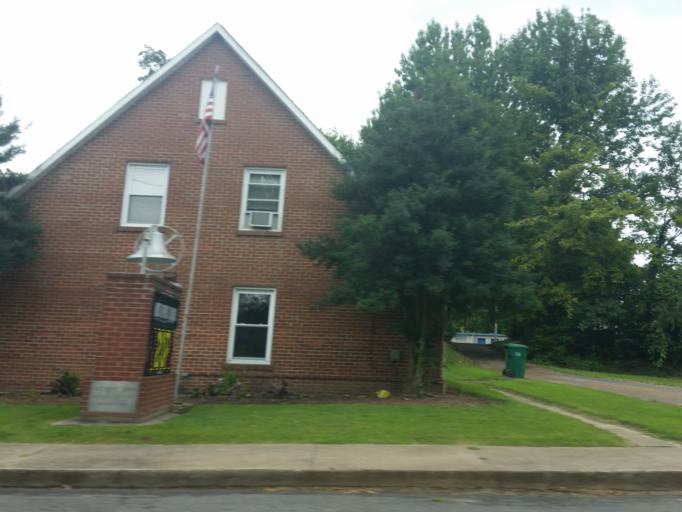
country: US
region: Kentucky
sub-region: Ballard County
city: Wickliffe
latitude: 36.9664
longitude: -89.0890
